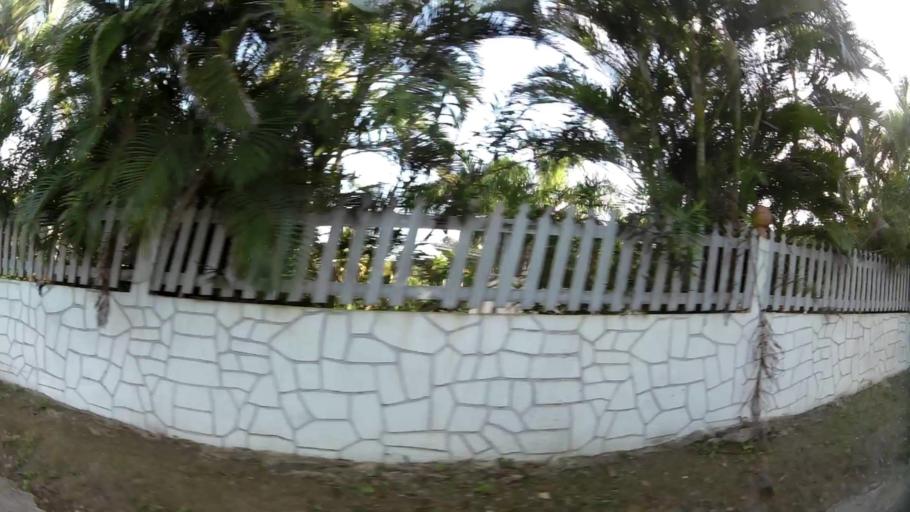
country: VG
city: Road Town
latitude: 18.4372
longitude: -64.6348
